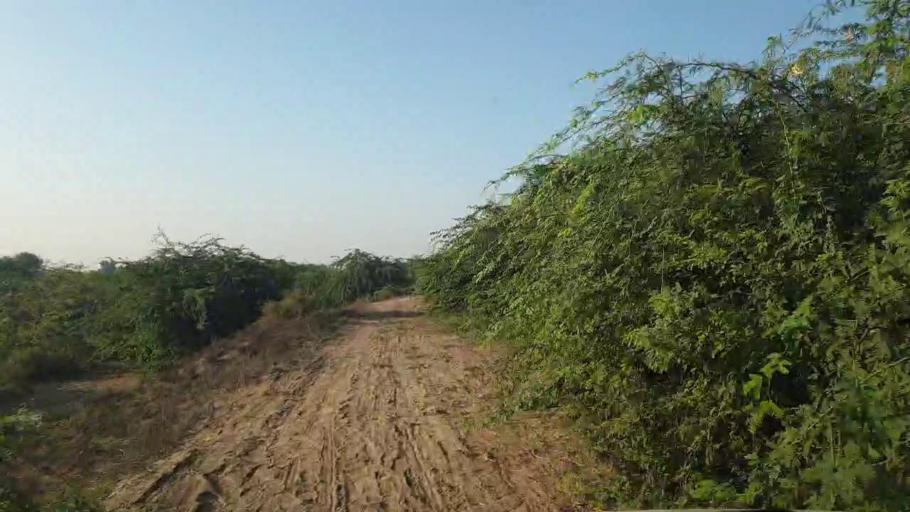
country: PK
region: Sindh
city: Badin
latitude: 24.6079
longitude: 68.7820
